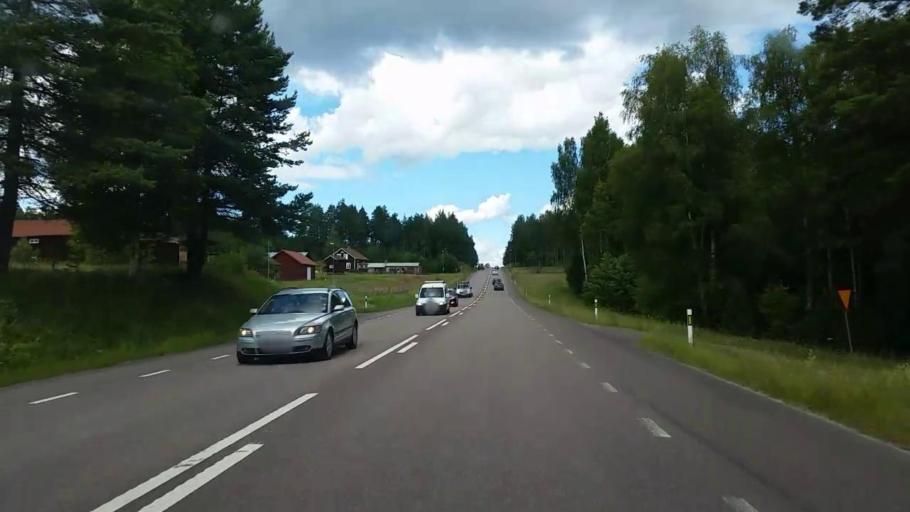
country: SE
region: Dalarna
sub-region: Gagnefs Kommun
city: Gagnef
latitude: 60.6340
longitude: 15.0578
